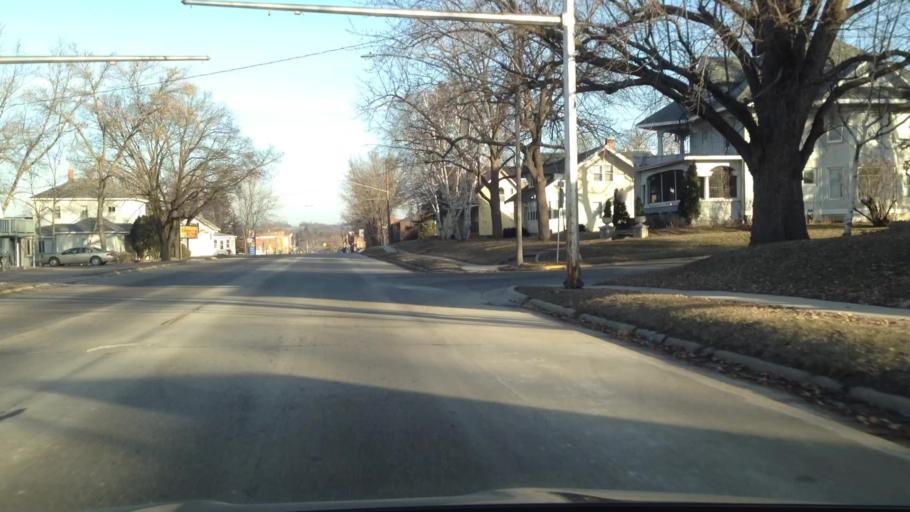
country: US
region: Minnesota
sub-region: Goodhue County
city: Zumbrota
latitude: 44.2905
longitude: -92.6692
